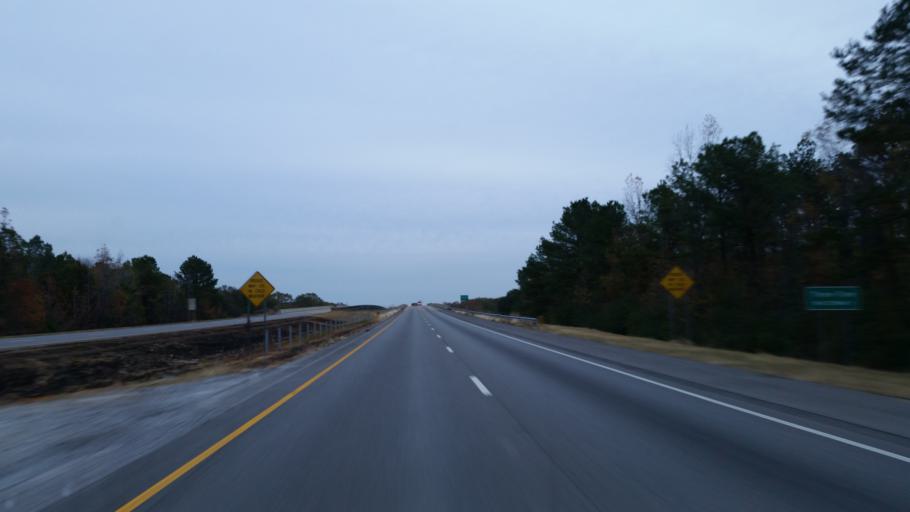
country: US
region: Alabama
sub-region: Sumter County
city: Livingston
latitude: 32.7340
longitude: -88.1030
